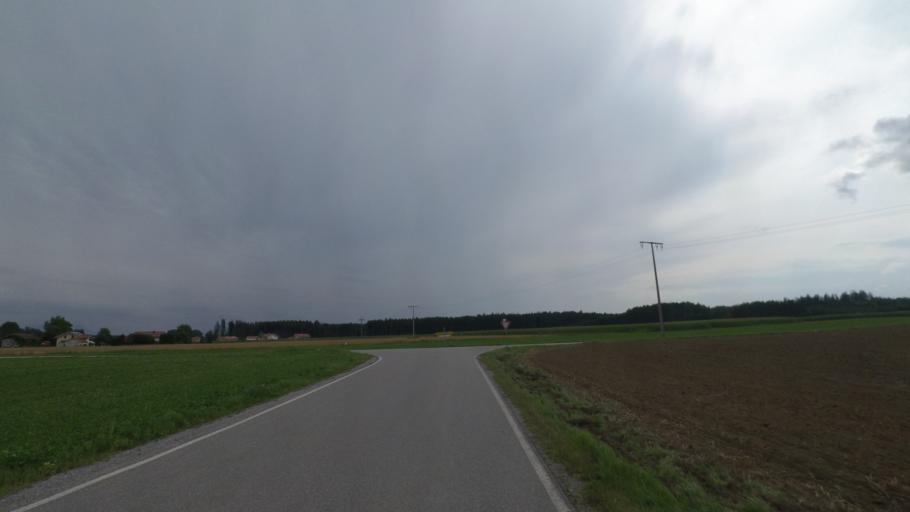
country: DE
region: Bavaria
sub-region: Upper Bavaria
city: Pittenhart
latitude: 47.9793
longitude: 12.3830
